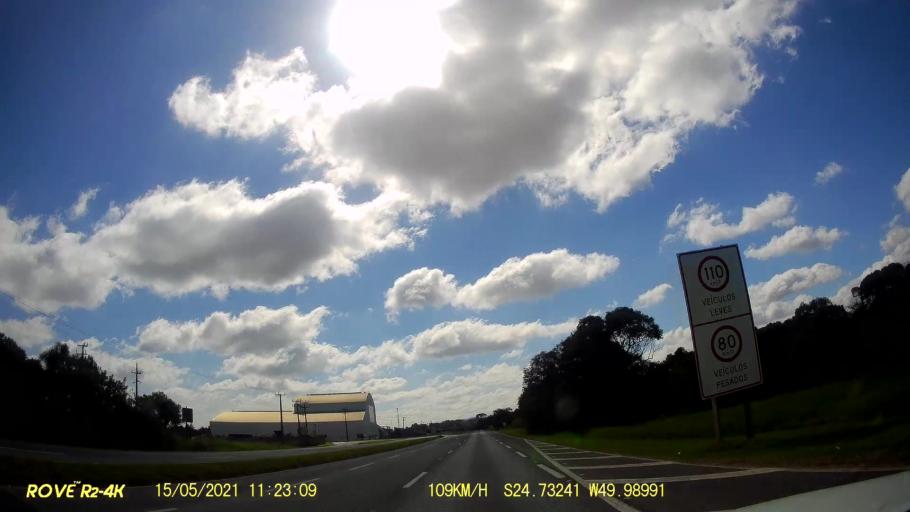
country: BR
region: Parana
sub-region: Castro
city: Castro
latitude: -24.7323
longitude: -49.9899
